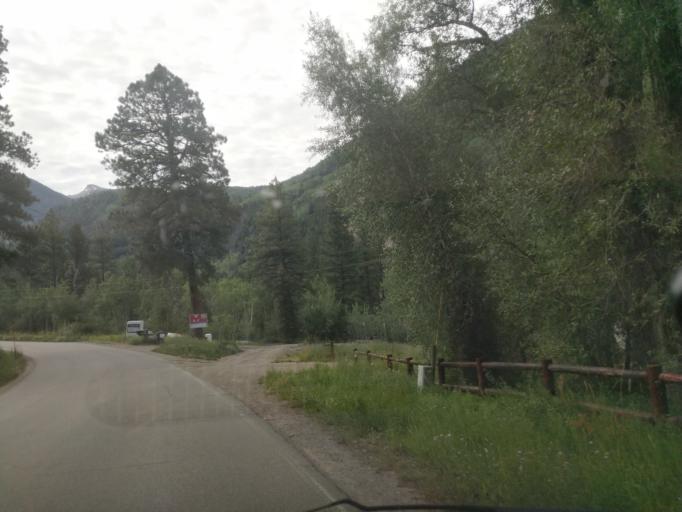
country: US
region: Colorado
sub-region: Gunnison County
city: Crested Butte
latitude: 39.0707
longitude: -107.1976
